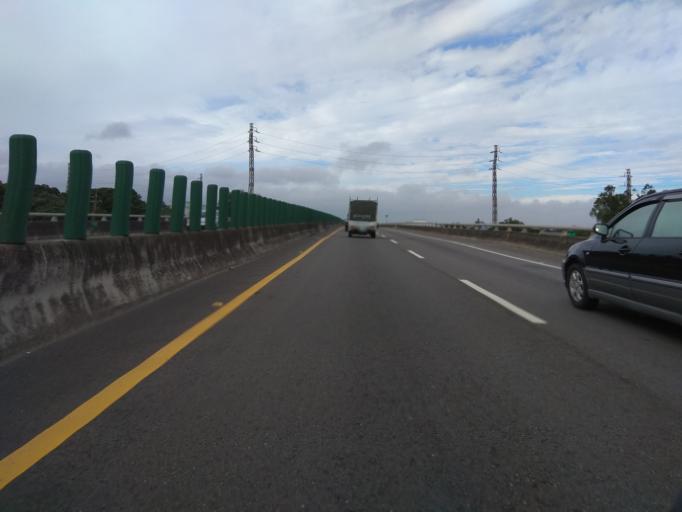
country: TW
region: Taiwan
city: Daxi
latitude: 24.8988
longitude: 121.2520
